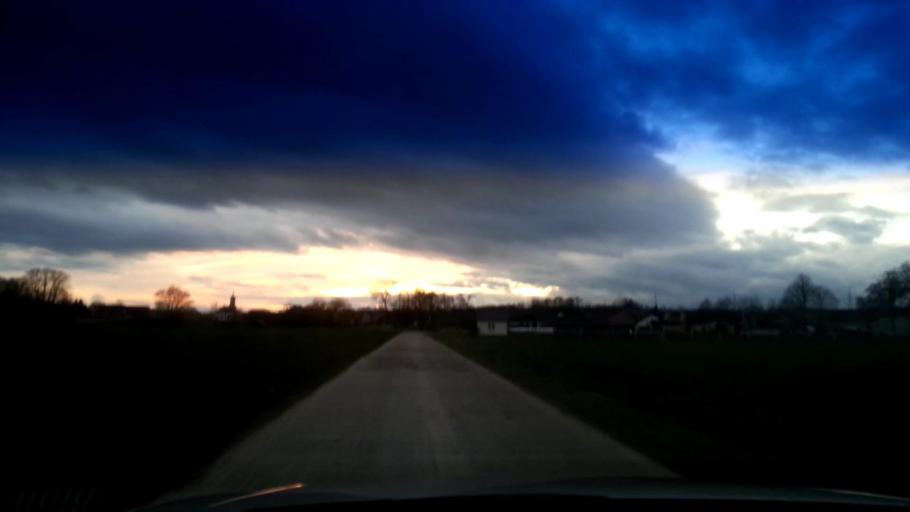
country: DE
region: Bavaria
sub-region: Upper Franconia
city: Schesslitz
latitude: 49.9633
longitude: 11.0025
